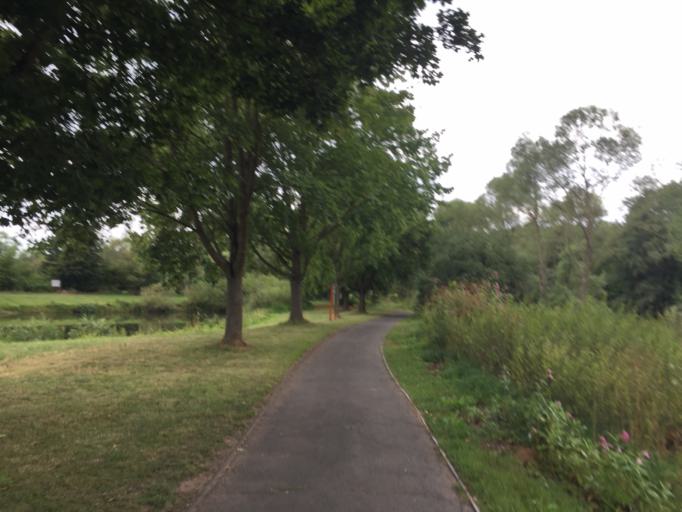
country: DE
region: Hesse
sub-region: Regierungsbezirk Kassel
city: Rotenburg an der Fulda
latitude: 50.9885
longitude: 9.7592
